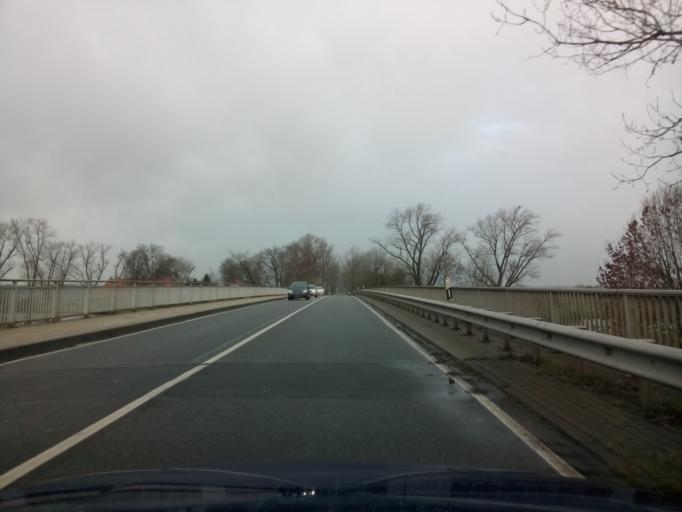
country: DE
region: Lower Saxony
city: Osterholz-Scharmbeck
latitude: 53.2023
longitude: 8.8205
